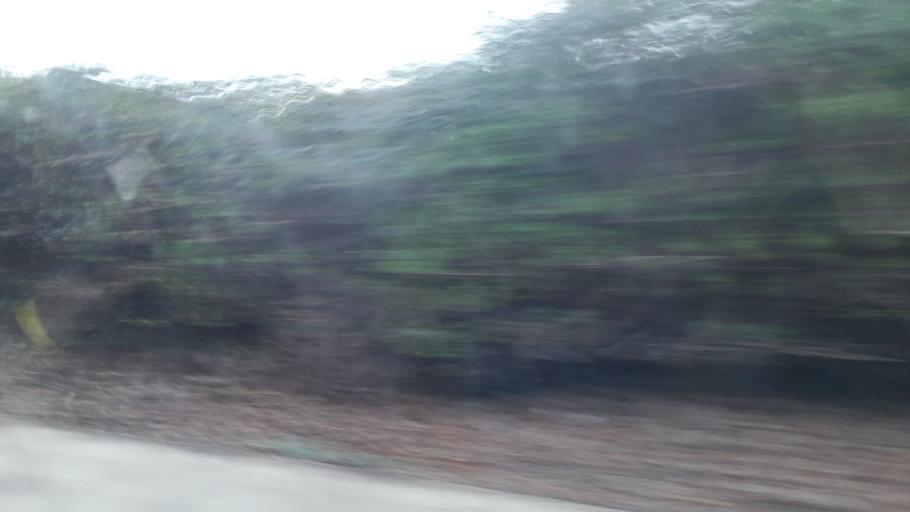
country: IE
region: Leinster
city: Lusk
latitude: 53.5197
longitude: -6.1360
